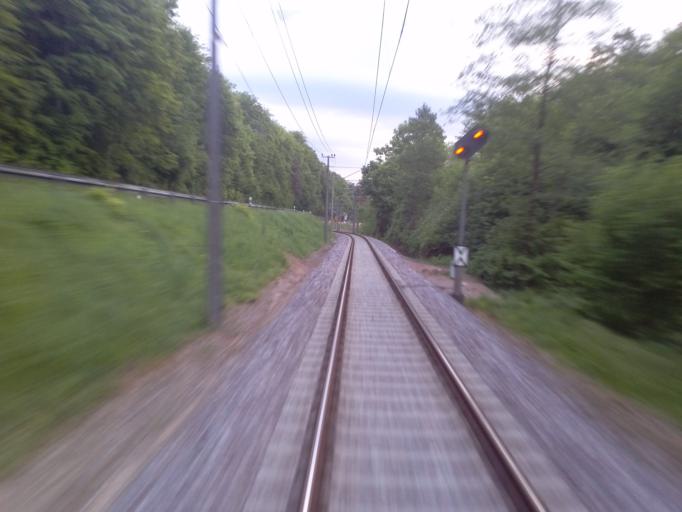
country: DE
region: Baden-Wuerttemberg
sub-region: Karlsruhe Region
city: Ettlingen
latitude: 48.8933
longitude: 8.4499
